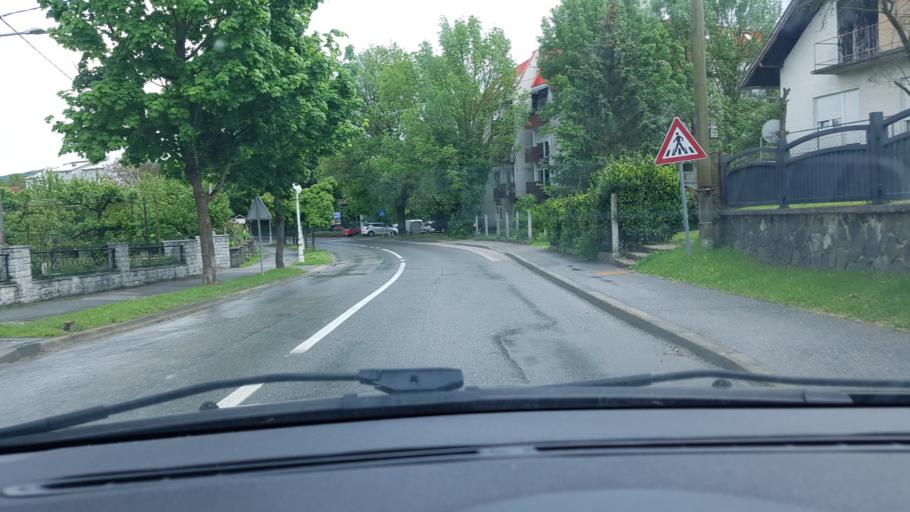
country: HR
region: Krapinsko-Zagorska
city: Oroslavje
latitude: 45.9784
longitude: 15.9299
